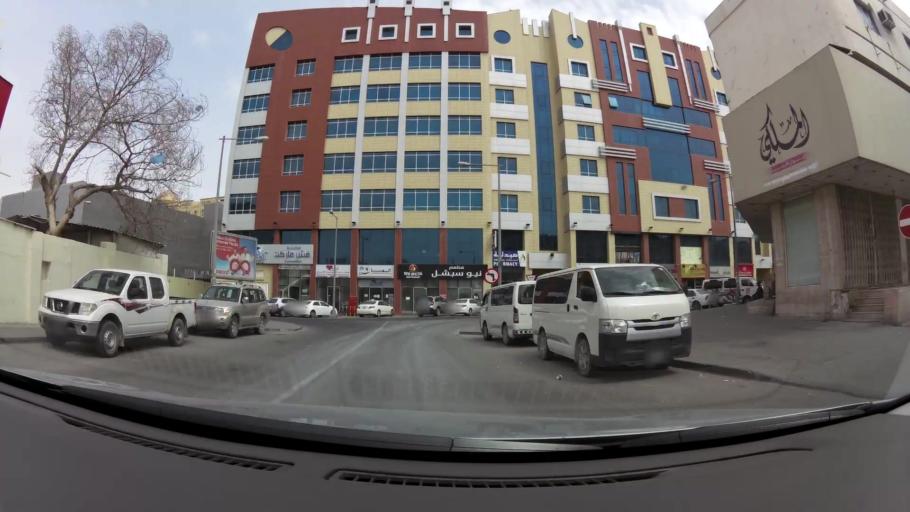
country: QA
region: Baladiyat ad Dawhah
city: Doha
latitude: 25.2819
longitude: 51.4967
